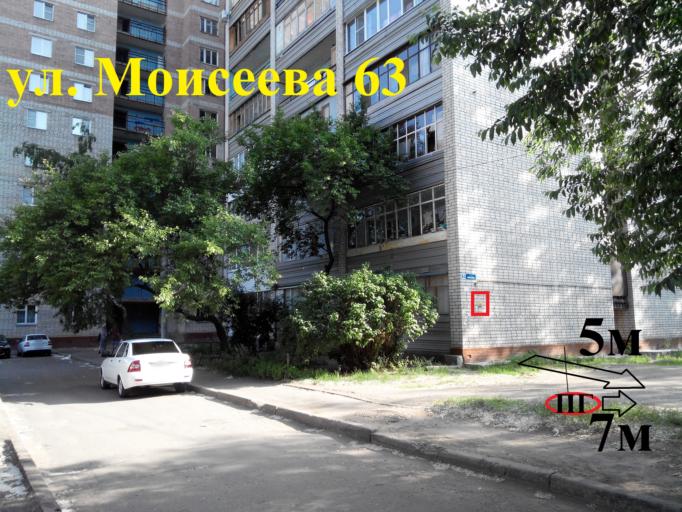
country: RU
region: Voronezj
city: Voronezh
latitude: 51.6498
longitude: 39.1762
